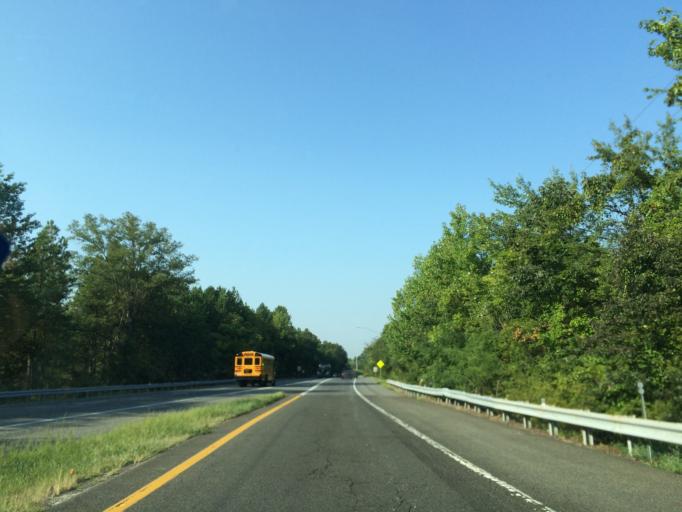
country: US
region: Maryland
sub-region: Anne Arundel County
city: Gambrills
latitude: 39.0628
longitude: -76.6497
